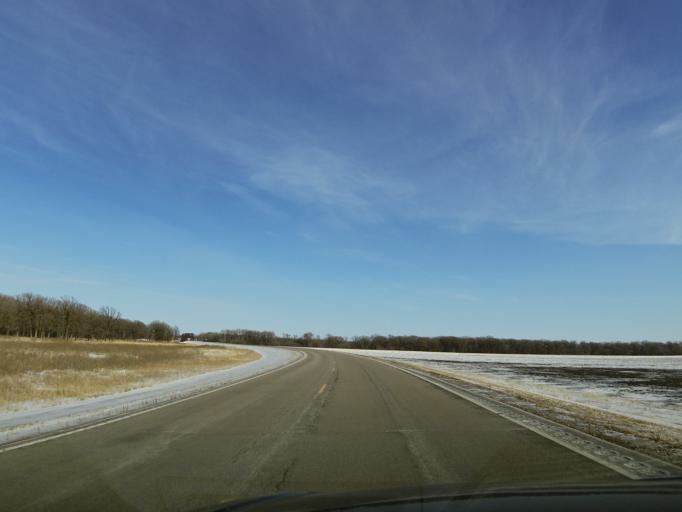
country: US
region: North Dakota
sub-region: Walsh County
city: Grafton
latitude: 48.4103
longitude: -97.1466
